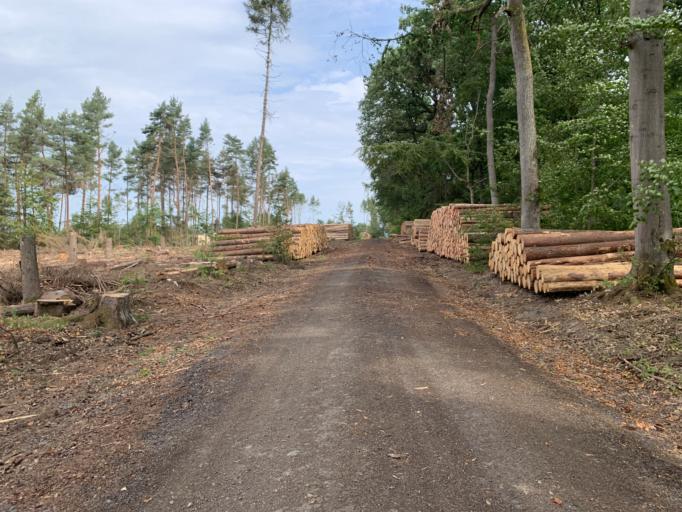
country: DE
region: Rheinland-Pfalz
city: Rettert
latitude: 50.2221
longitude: 7.9463
